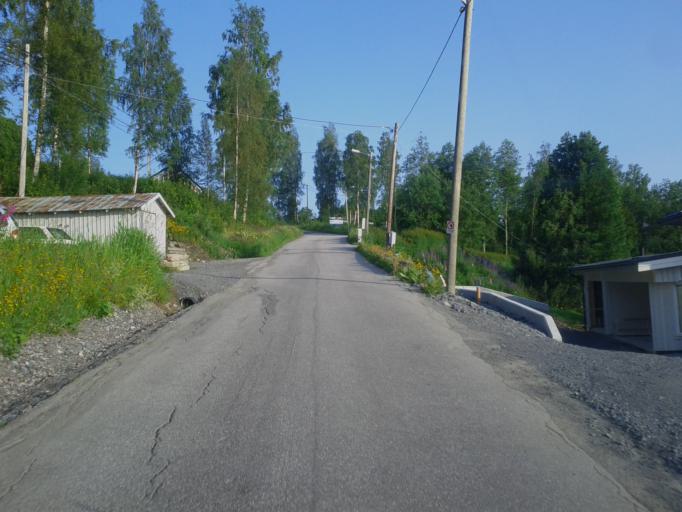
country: SE
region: Vaesternorrland
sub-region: OErnskoeldsviks Kommun
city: Ornskoldsvik
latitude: 63.2583
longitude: 18.8089
